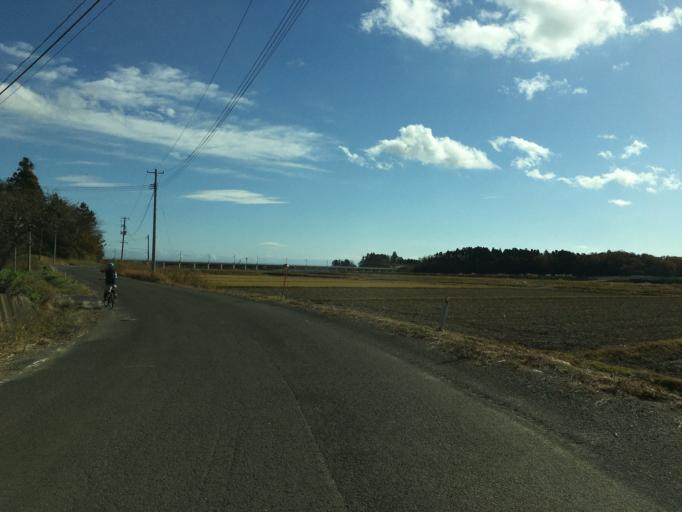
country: JP
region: Miyagi
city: Marumori
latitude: 37.8930
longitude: 140.9156
